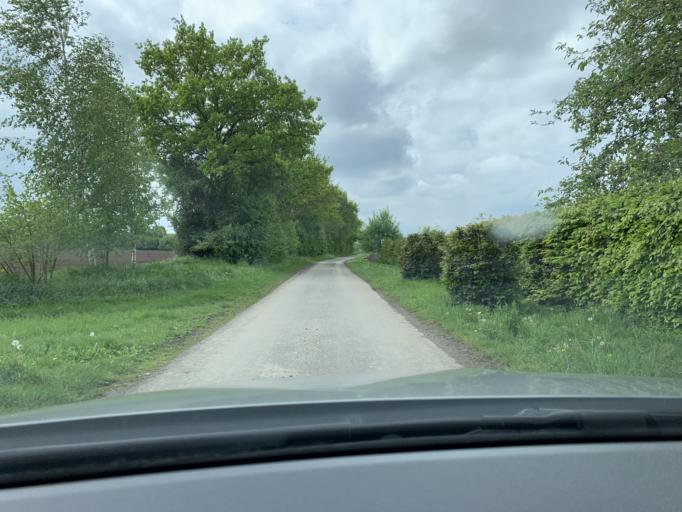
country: DE
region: North Rhine-Westphalia
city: Rietberg
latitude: 51.7910
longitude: 8.3782
